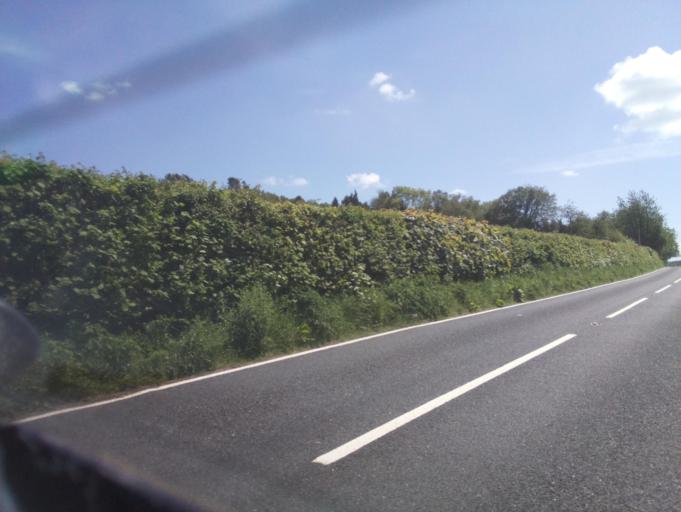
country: GB
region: Wales
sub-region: Monmouthshire
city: Mitchel Troy
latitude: 51.7600
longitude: -2.7235
